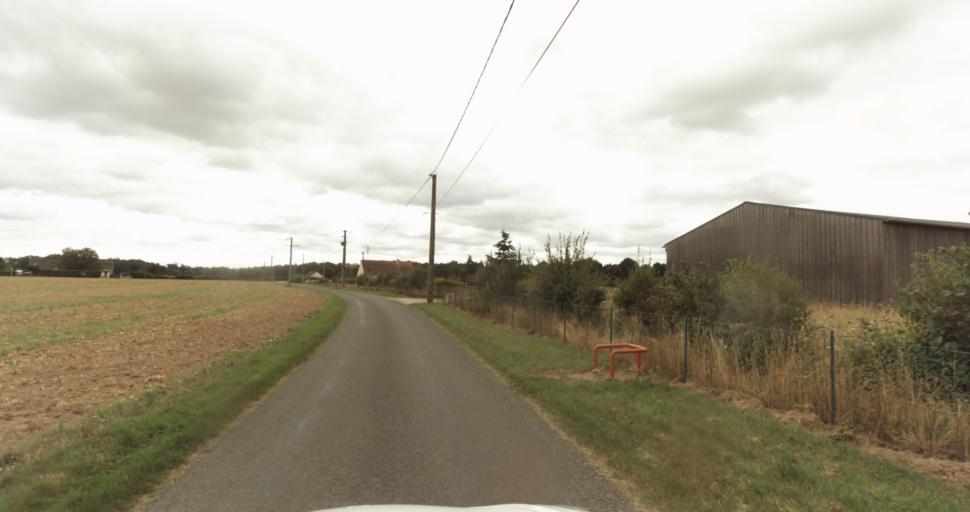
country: FR
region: Haute-Normandie
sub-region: Departement de l'Eure
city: La Madeleine-de-Nonancourt
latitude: 48.8118
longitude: 1.2115
